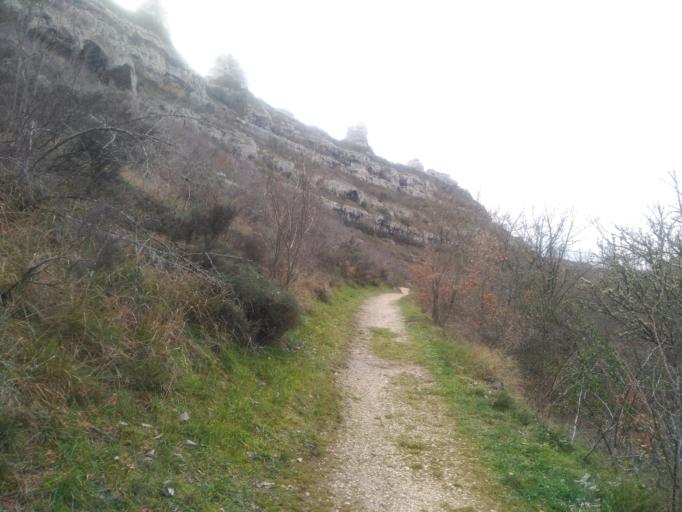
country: ES
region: Cantabria
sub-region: Provincia de Cantabria
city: San Martin de Elines
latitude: 42.8325
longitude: -3.7918
